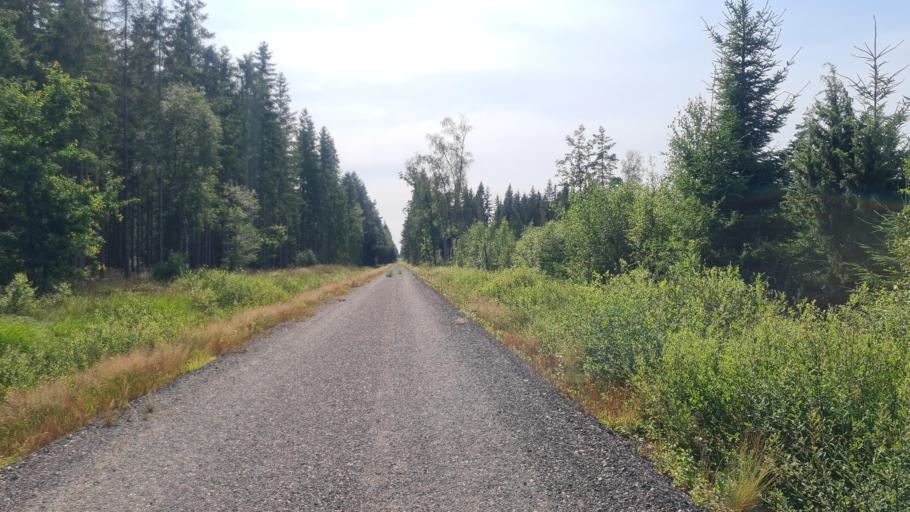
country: SE
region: Kronoberg
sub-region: Ljungby Kommun
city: Lagan
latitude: 56.9817
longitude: 13.9455
